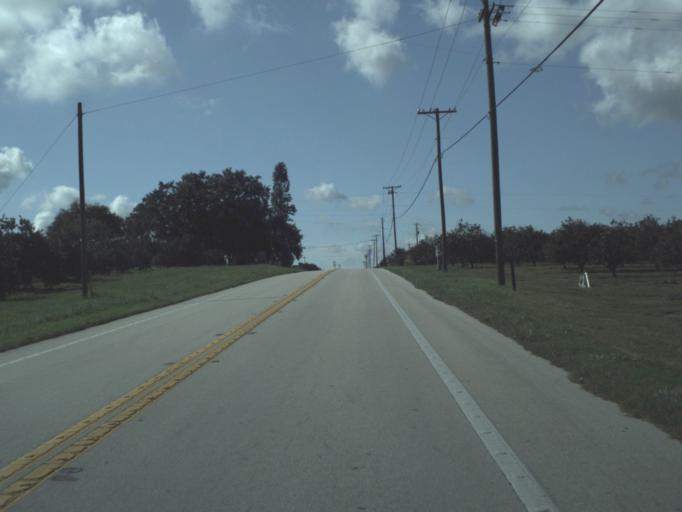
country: US
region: Florida
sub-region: Polk County
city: Frostproof
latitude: 27.7236
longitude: -81.5310
